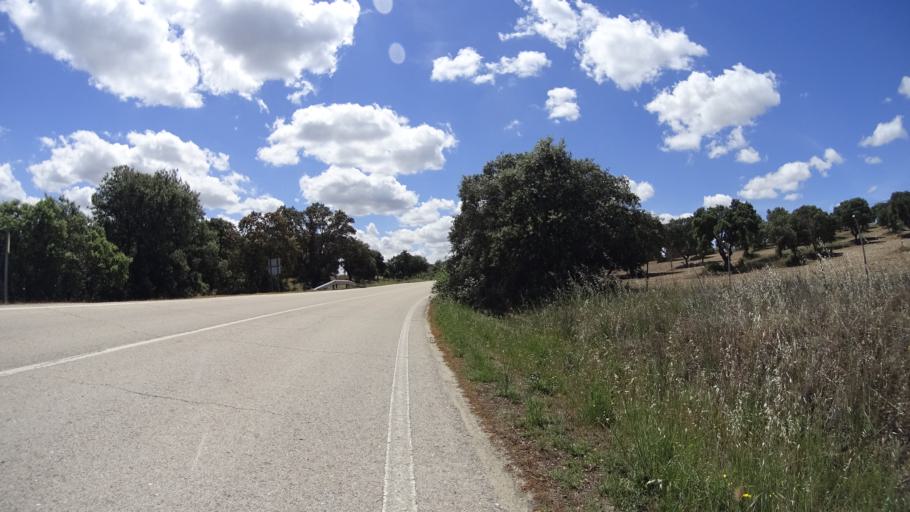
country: ES
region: Madrid
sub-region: Provincia de Madrid
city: Villanueva del Pardillo
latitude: 40.4507
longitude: -3.9532
